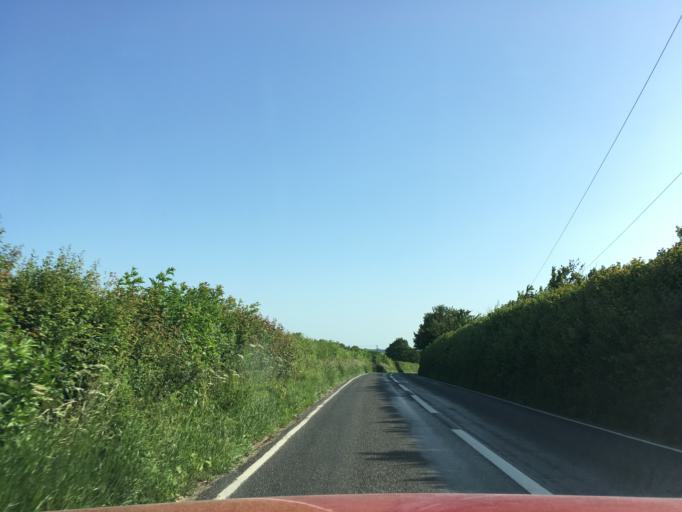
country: GB
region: England
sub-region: Oxfordshire
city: Stonesfield
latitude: 51.9254
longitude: -1.4050
